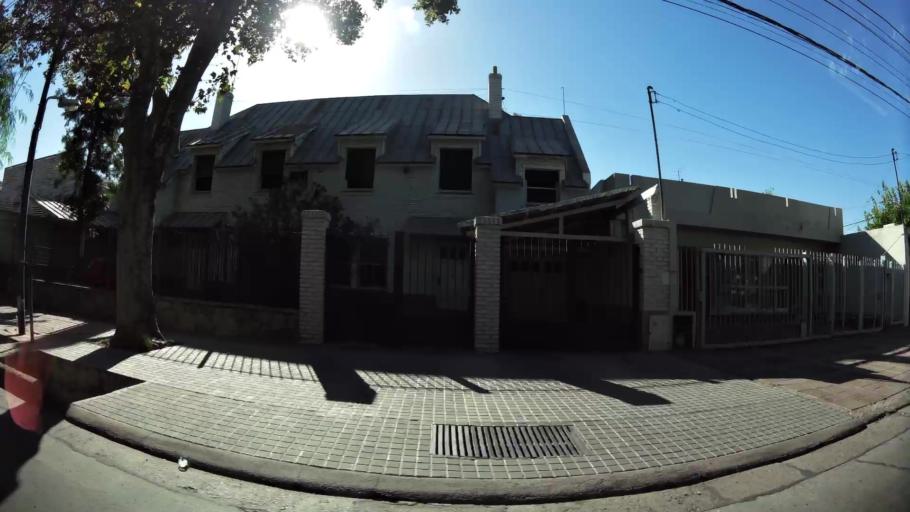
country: AR
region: Mendoza
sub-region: Departamento de Godoy Cruz
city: Godoy Cruz
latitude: -32.9146
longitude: -68.8425
